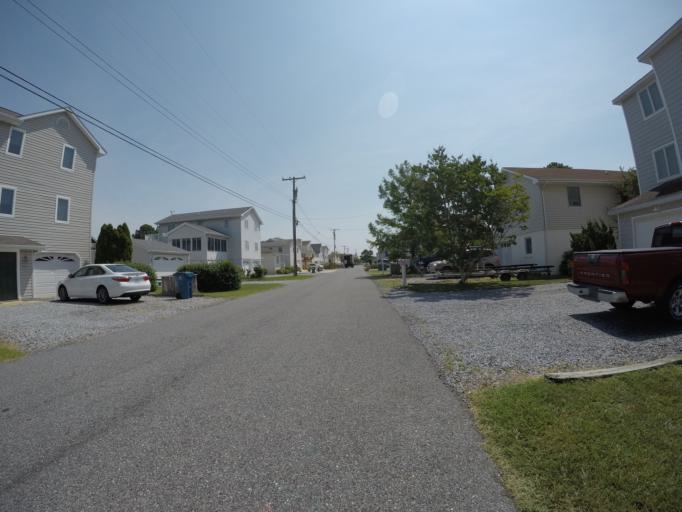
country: US
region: Delaware
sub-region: Sussex County
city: Bethany Beach
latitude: 38.5183
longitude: -75.0593
